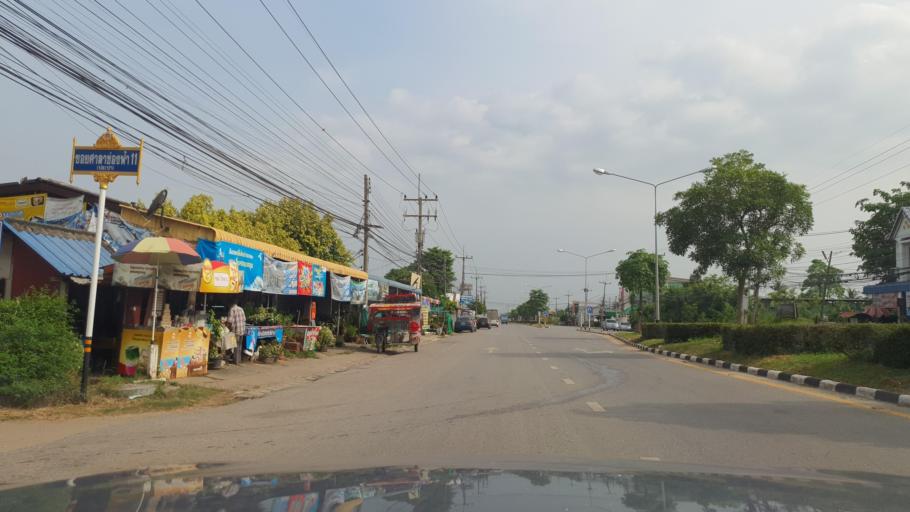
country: TH
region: Phitsanulok
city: Phitsanulok
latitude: 16.8585
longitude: 100.2522
